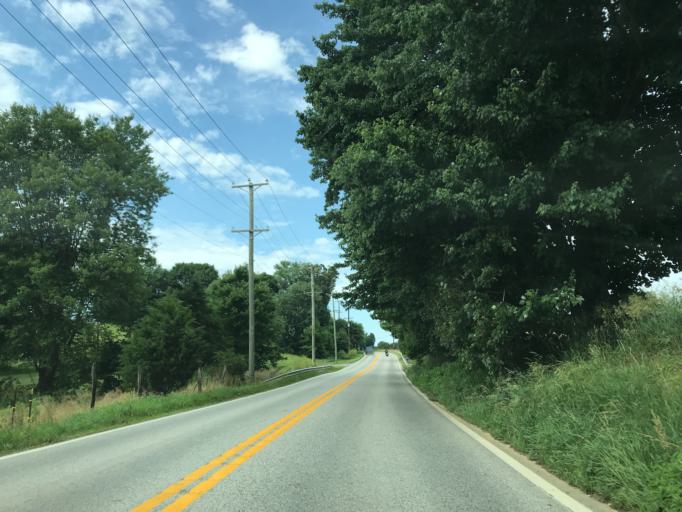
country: US
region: Maryland
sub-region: Harford County
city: Jarrettsville
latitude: 39.6602
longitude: -76.4078
